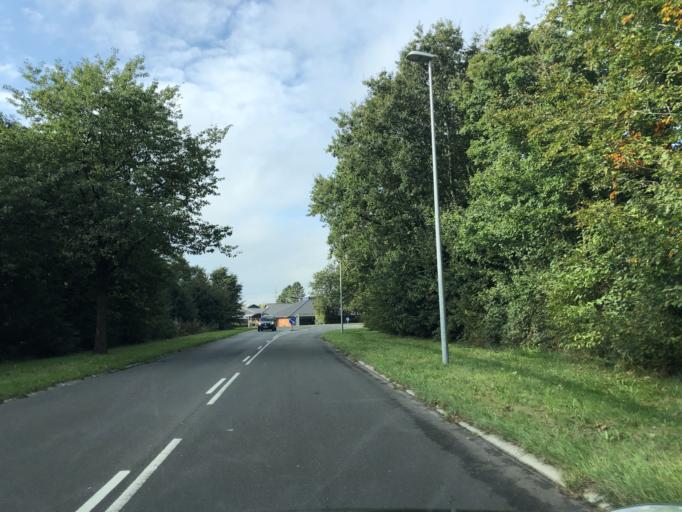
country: DK
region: Central Jutland
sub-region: Holstebro Kommune
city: Holstebro
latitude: 56.3685
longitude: 8.5902
